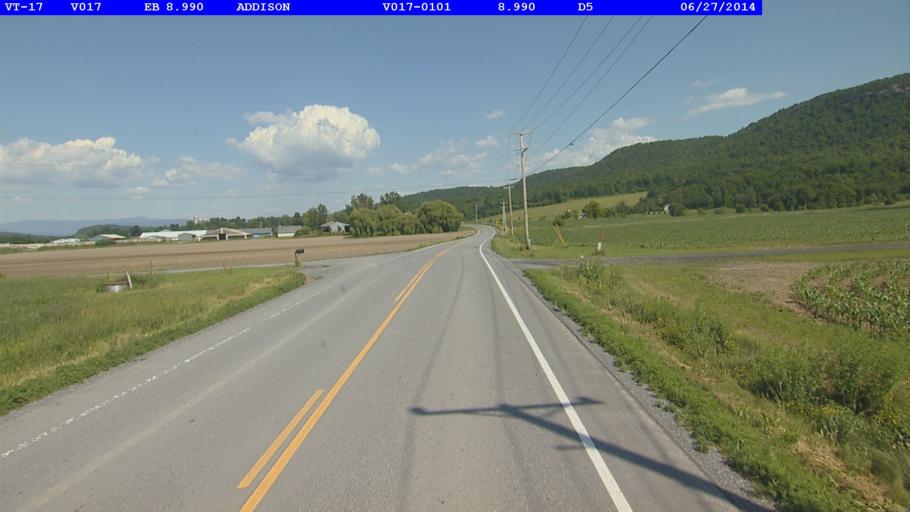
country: US
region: Vermont
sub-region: Addison County
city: Vergennes
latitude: 44.0858
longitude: -73.2910
